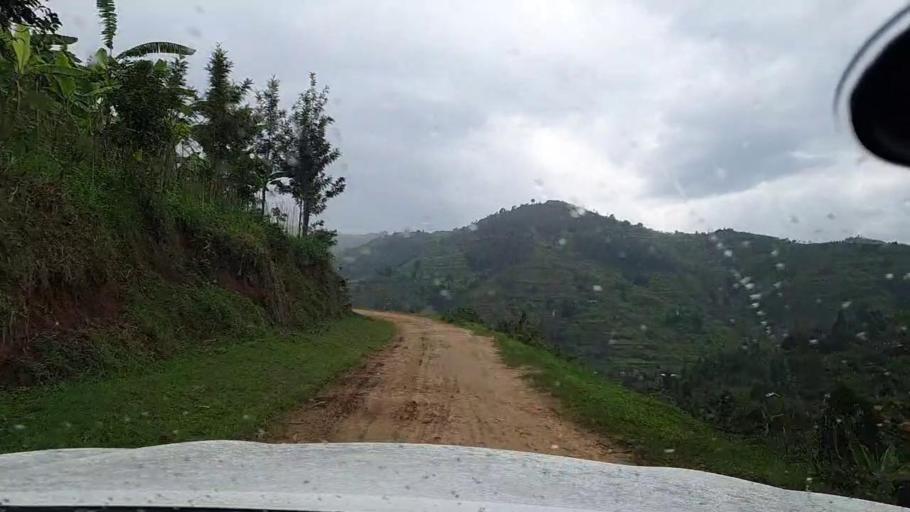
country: RW
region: Western Province
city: Kibuye
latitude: -2.0773
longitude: 29.4444
